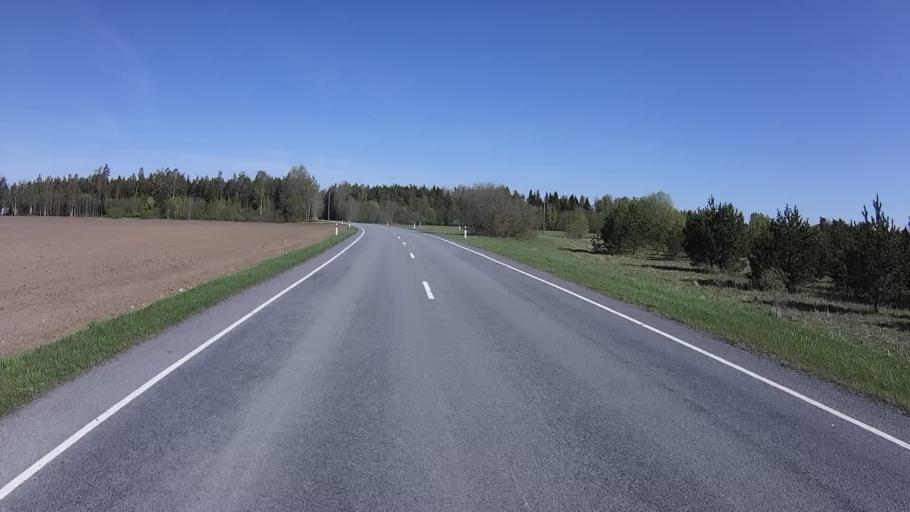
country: EE
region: Raplamaa
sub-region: Jaervakandi vald
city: Jarvakandi
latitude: 58.8479
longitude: 24.7958
